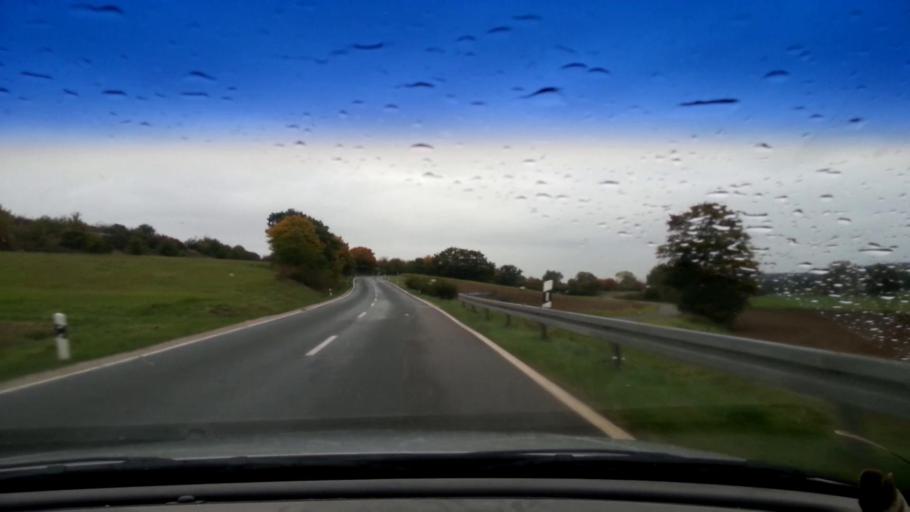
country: DE
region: Bavaria
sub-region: Upper Franconia
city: Priesendorf
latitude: 49.8609
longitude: 10.6787
